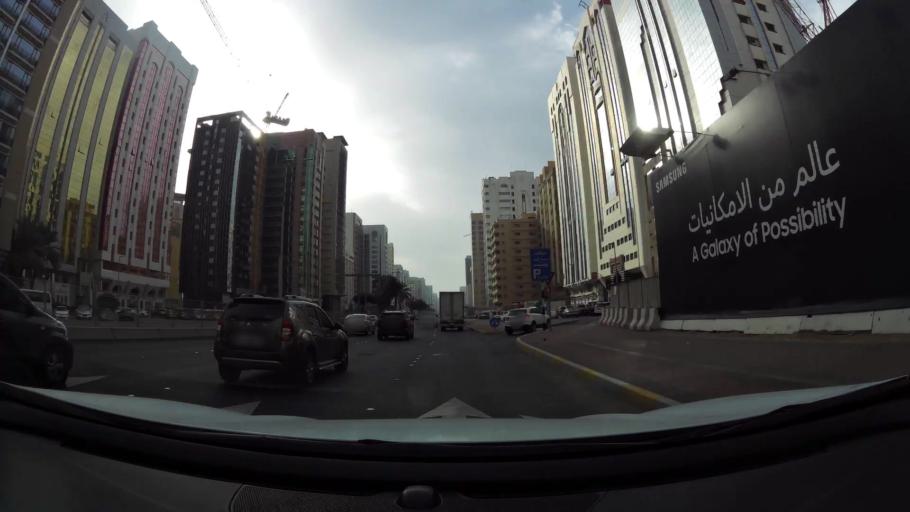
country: AE
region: Abu Dhabi
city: Abu Dhabi
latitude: 24.4690
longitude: 54.3715
